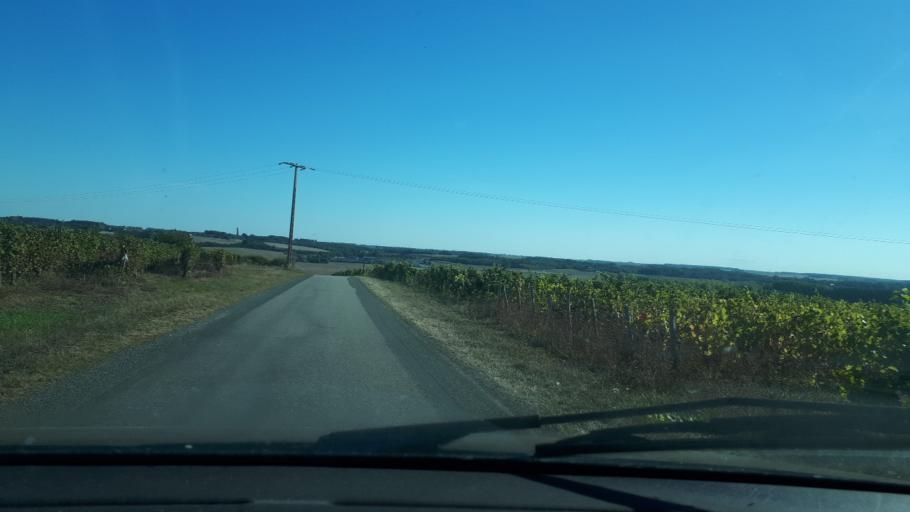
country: FR
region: Centre
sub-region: Departement du Loir-et-Cher
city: Naveil
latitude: 47.8000
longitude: 1.0186
